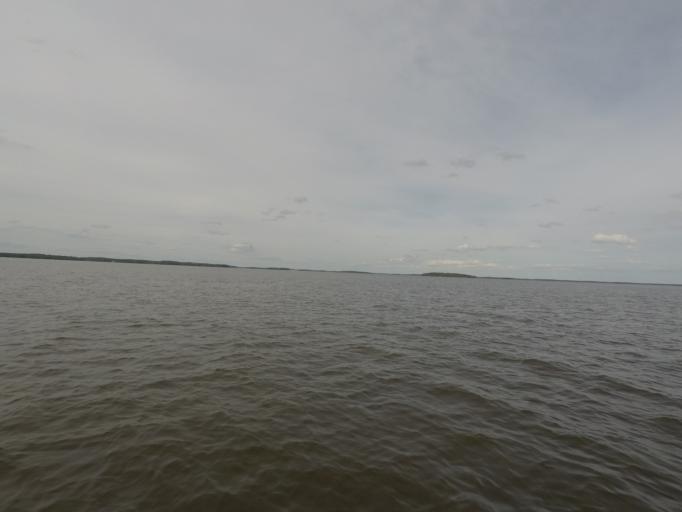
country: SE
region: Soedermanland
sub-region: Eskilstuna Kommun
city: Torshalla
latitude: 59.4616
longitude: 16.4733
